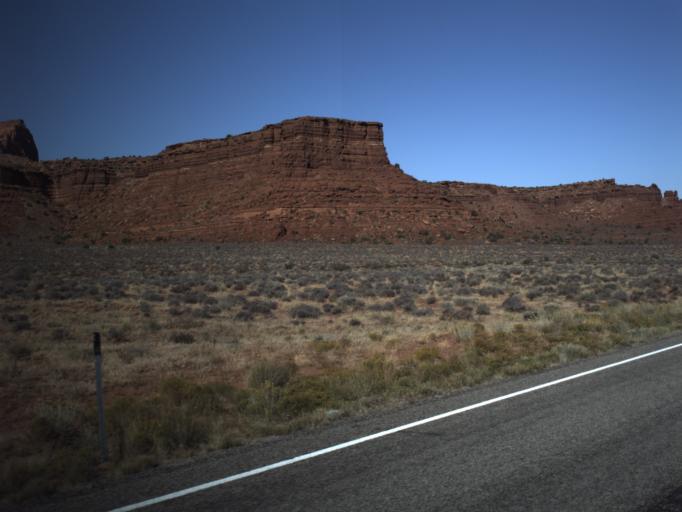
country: US
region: Utah
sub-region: San Juan County
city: Blanding
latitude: 37.7919
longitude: -110.3000
